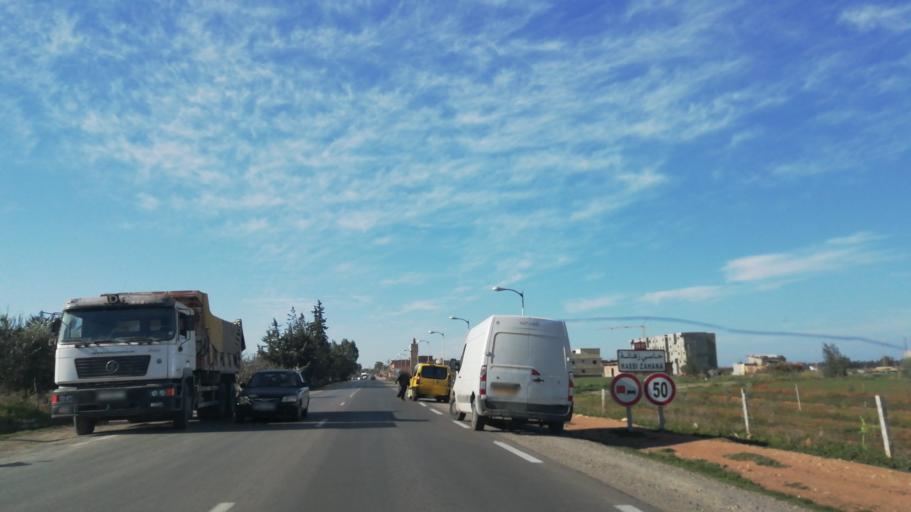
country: DZ
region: Tlemcen
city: Ouled Mimoun
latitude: 35.0285
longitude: -0.8761
